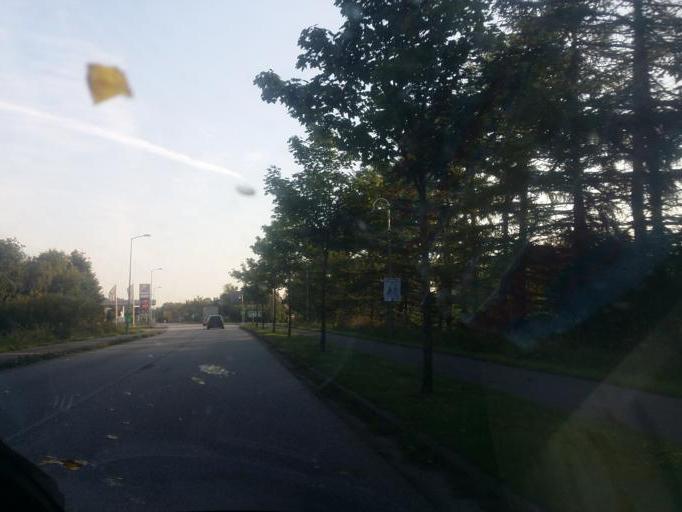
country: DE
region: Schleswig-Holstein
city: Bargum
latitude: 54.6841
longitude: 8.9571
